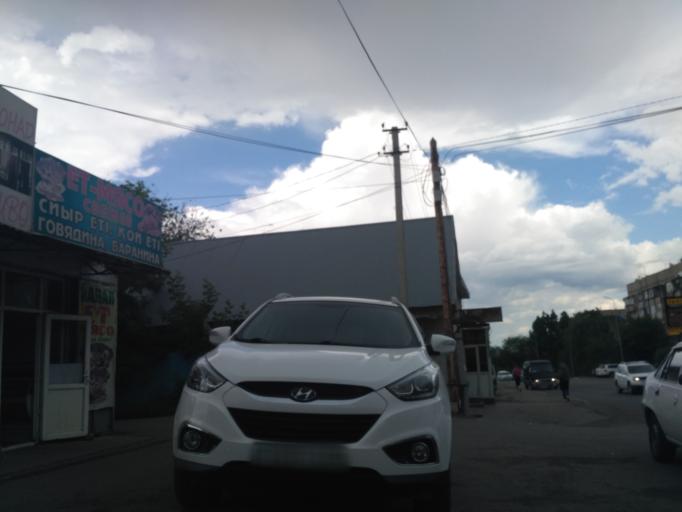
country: KZ
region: Almaty Oblysy
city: Burunday
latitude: 43.2031
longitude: 76.6352
